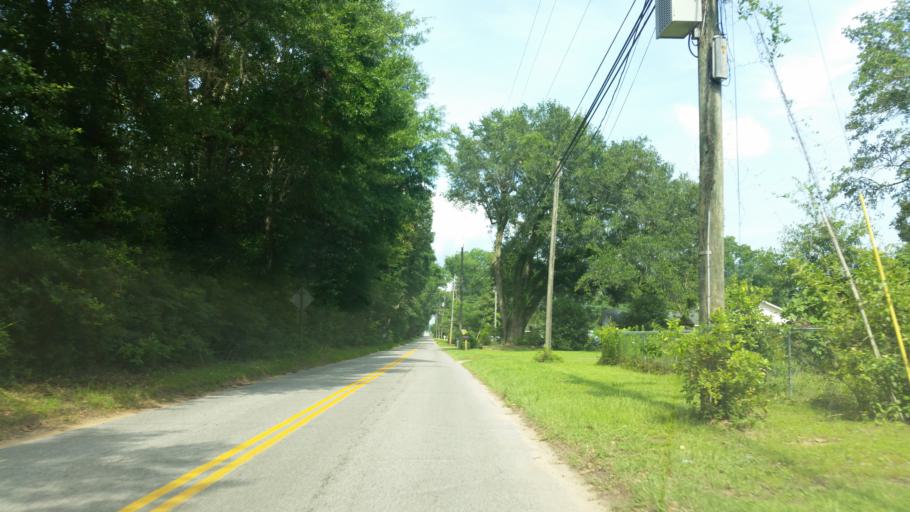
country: US
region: Florida
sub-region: Escambia County
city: Cantonment
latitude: 30.5786
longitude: -87.3576
